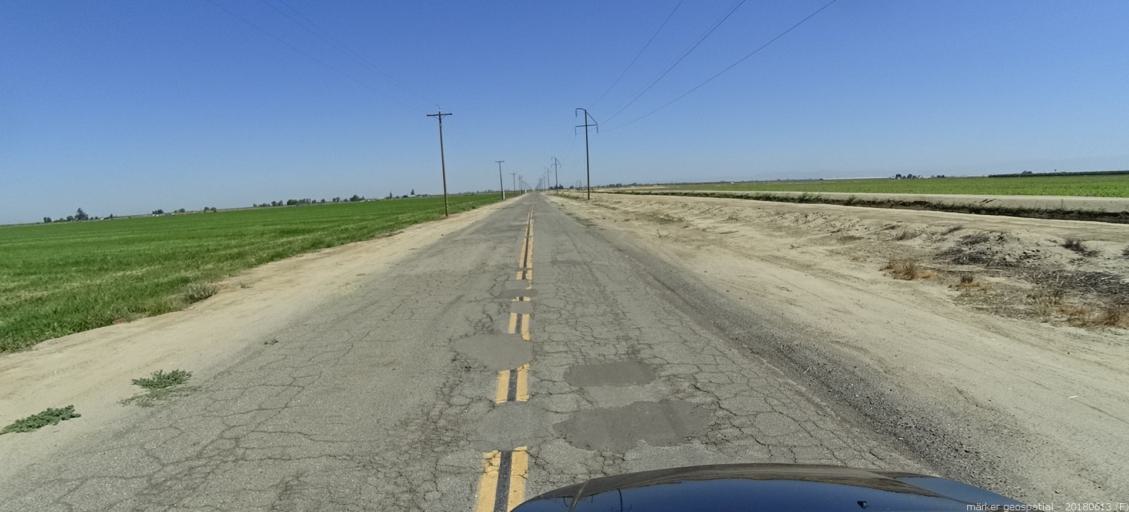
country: US
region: California
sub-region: Madera County
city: Chowchilla
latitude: 37.0764
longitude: -120.3469
